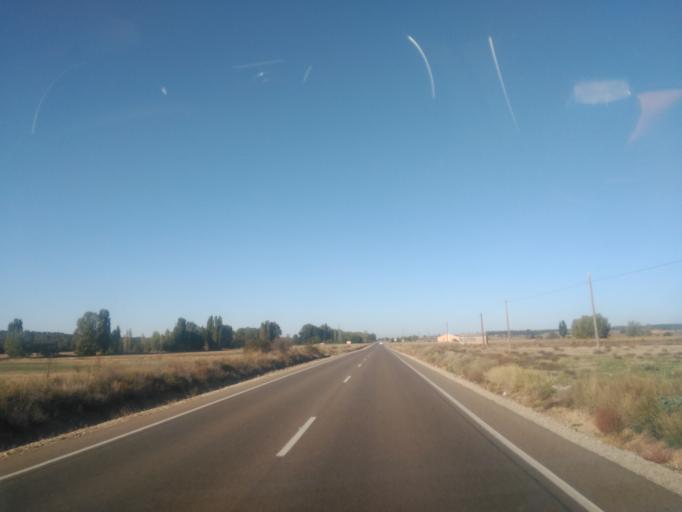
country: ES
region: Castille and Leon
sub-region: Provincia de Burgos
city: Quemada
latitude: 41.6912
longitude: -3.5991
